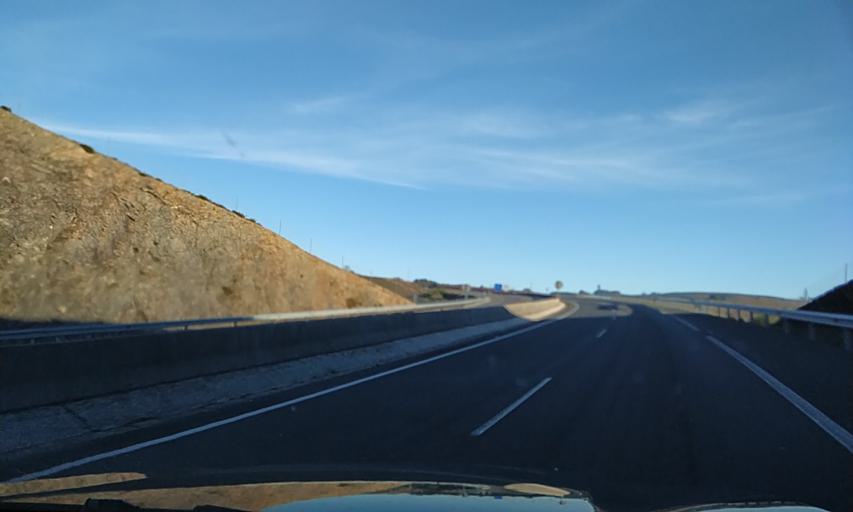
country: ES
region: Galicia
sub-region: Provincia de Pontevedra
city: Dozon
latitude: 42.5816
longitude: -8.0691
